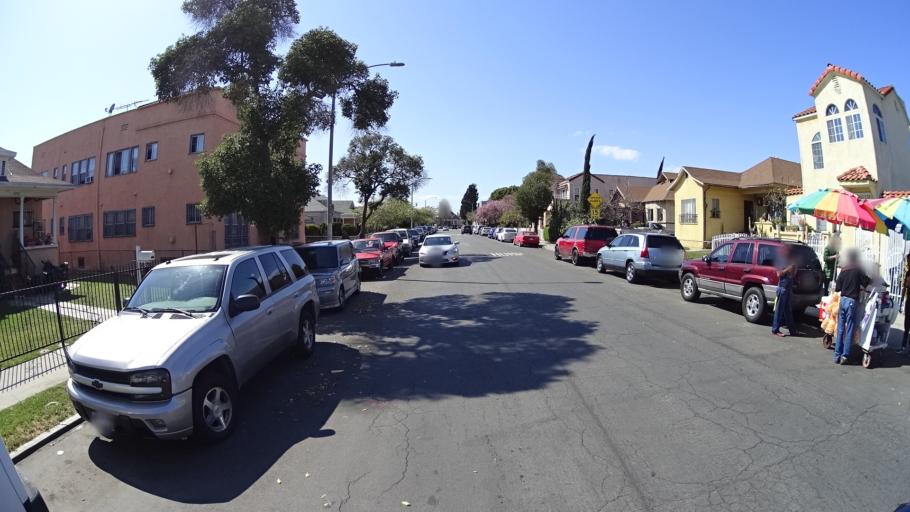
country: US
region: California
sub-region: Los Angeles County
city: Boyle Heights
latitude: 34.0469
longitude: -118.2055
